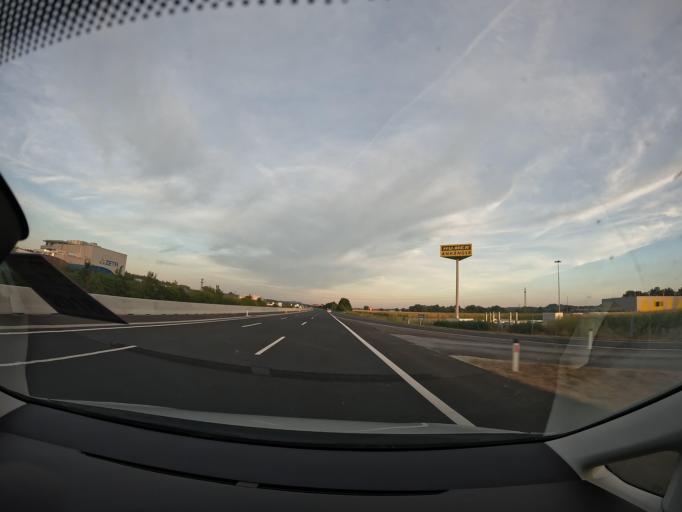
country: AT
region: Styria
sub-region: Politischer Bezirk Graz-Umgebung
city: Lieboch
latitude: 46.9687
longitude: 15.3496
